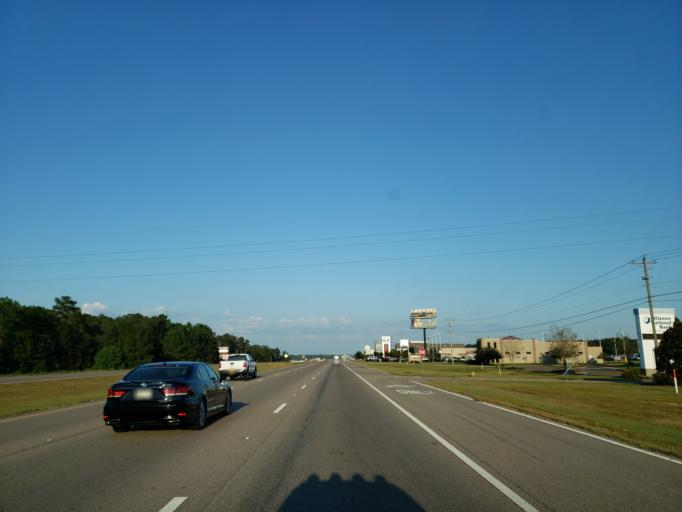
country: US
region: Mississippi
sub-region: Lamar County
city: West Hattiesburg
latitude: 31.3191
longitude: -89.3973
